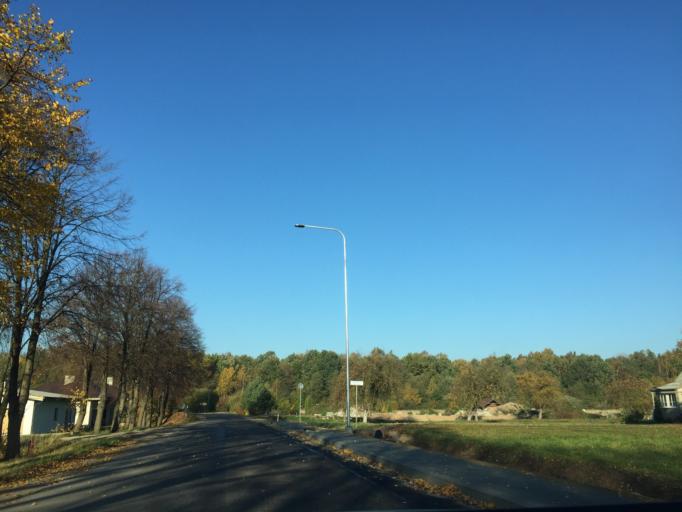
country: LT
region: Klaipedos apskritis
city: Kretinga
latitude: 55.8925
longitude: 21.2125
